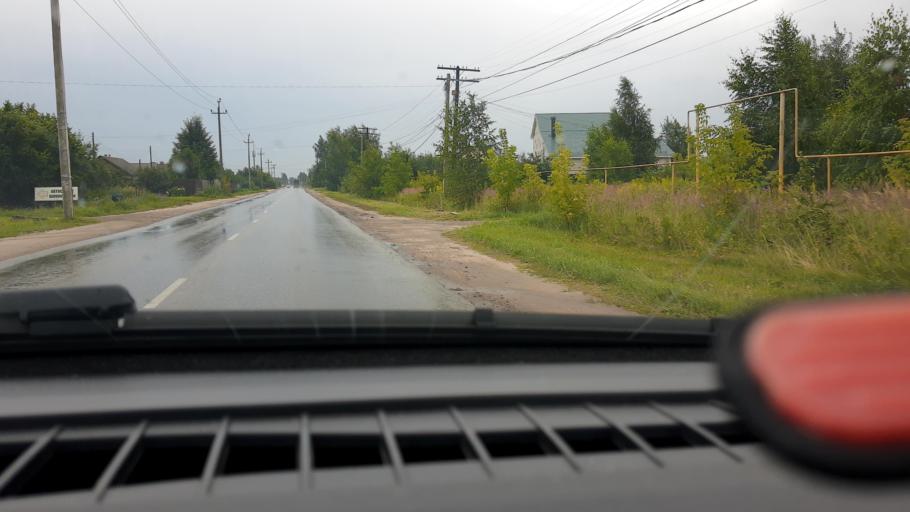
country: RU
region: Nizjnij Novgorod
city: Bor
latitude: 56.3538
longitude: 44.1067
